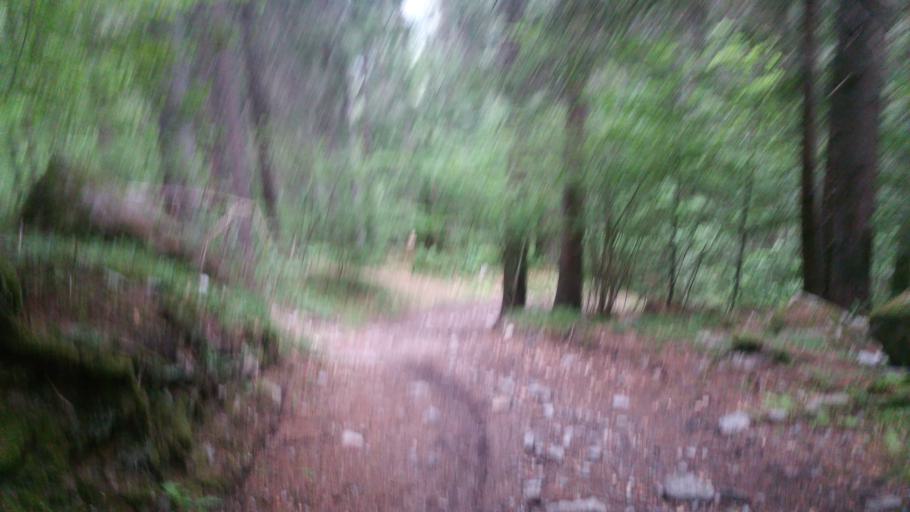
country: FR
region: Rhone-Alpes
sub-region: Departement de la Haute-Savoie
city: Les Houches
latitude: 45.9007
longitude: 6.8045
